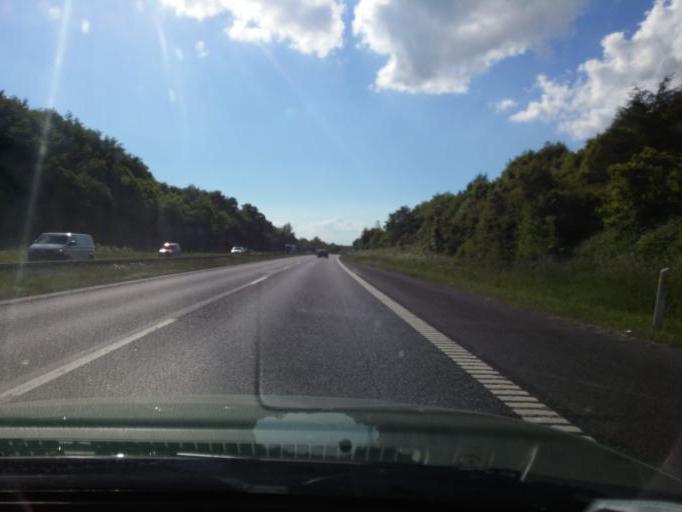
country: DK
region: South Denmark
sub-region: Assens Kommune
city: Arup
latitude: 55.4111
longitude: 10.0526
